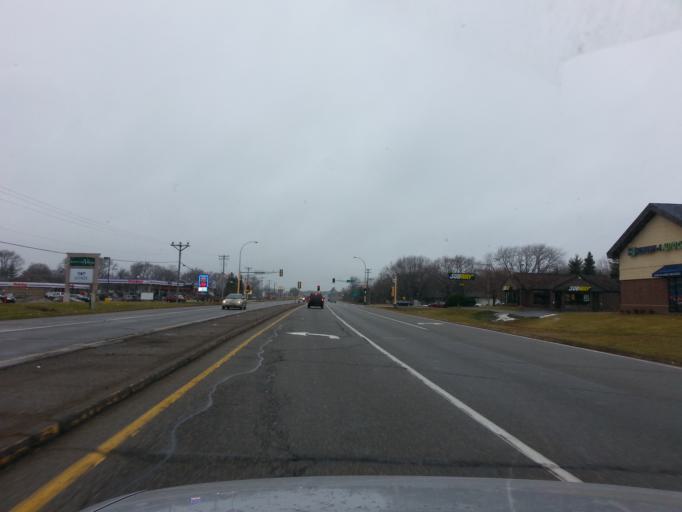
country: US
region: Minnesota
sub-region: Scott County
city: Prior Lake
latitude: 44.7074
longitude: -93.4289
